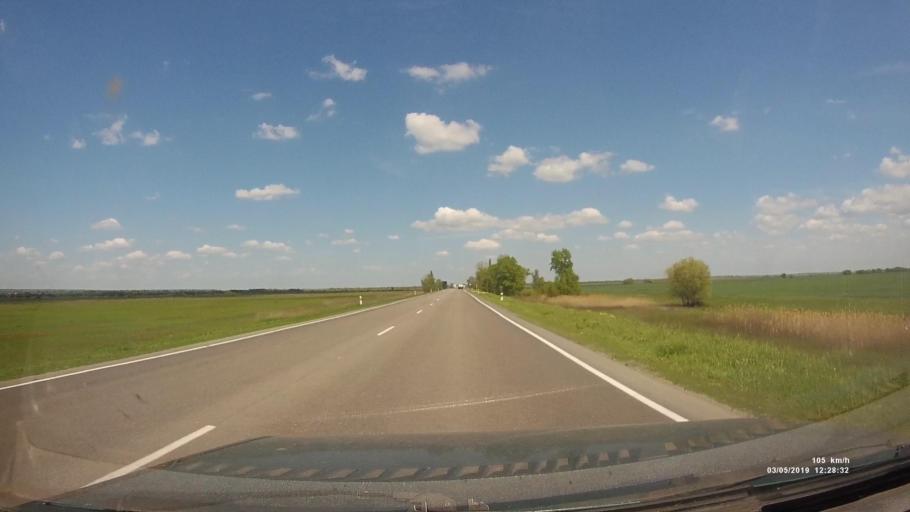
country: RU
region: Rostov
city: Semikarakorsk
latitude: 47.4750
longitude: 40.7301
